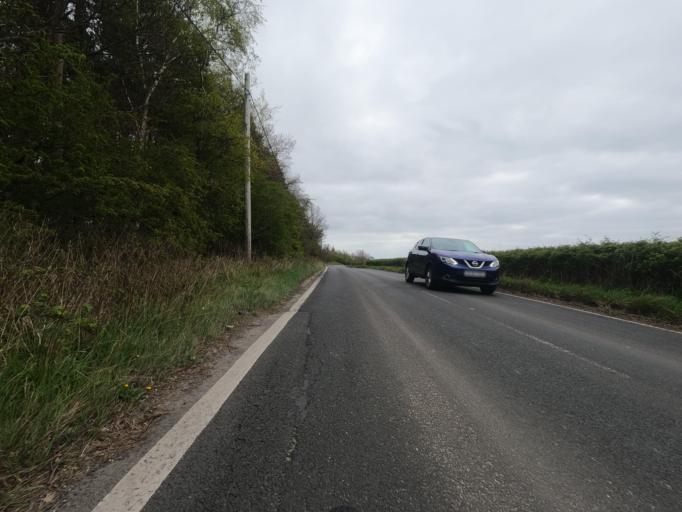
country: GB
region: England
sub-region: Newcastle upon Tyne
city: Dinnington
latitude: 55.0654
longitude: -1.6856
